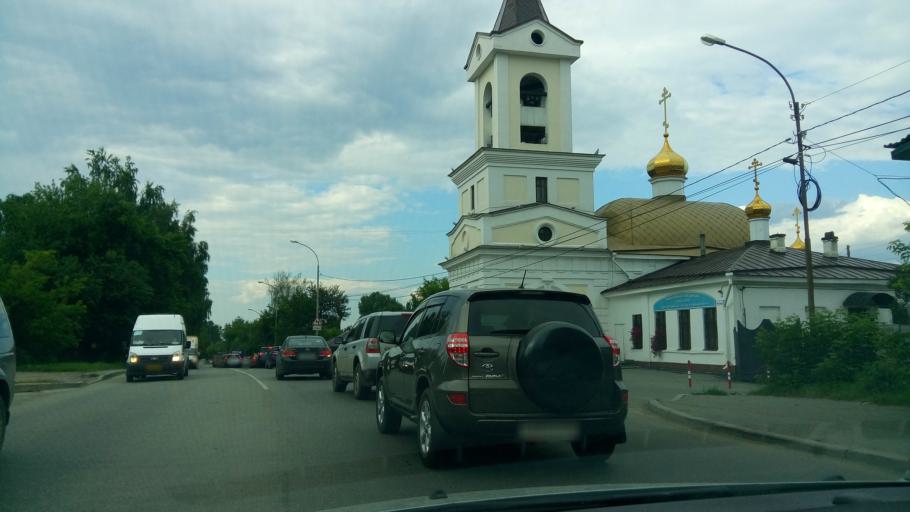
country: RU
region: Sverdlovsk
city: Yekaterinburg
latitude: 56.8757
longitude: 60.6911
